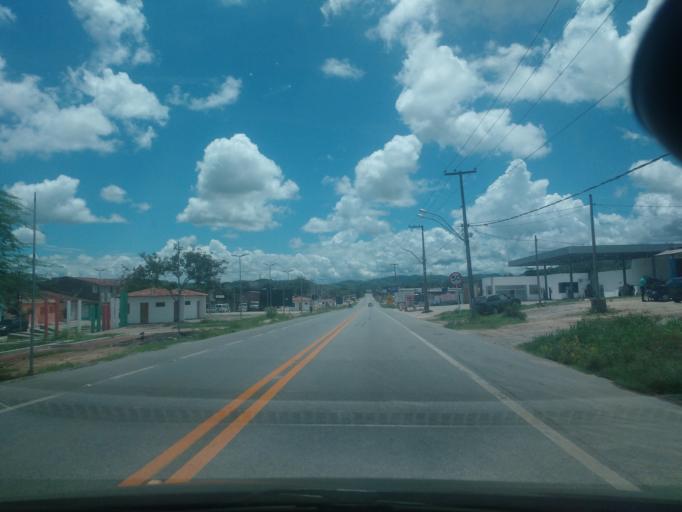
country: BR
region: Alagoas
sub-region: Uniao Dos Palmares
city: Uniao dos Palmares
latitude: -9.1648
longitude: -36.0196
